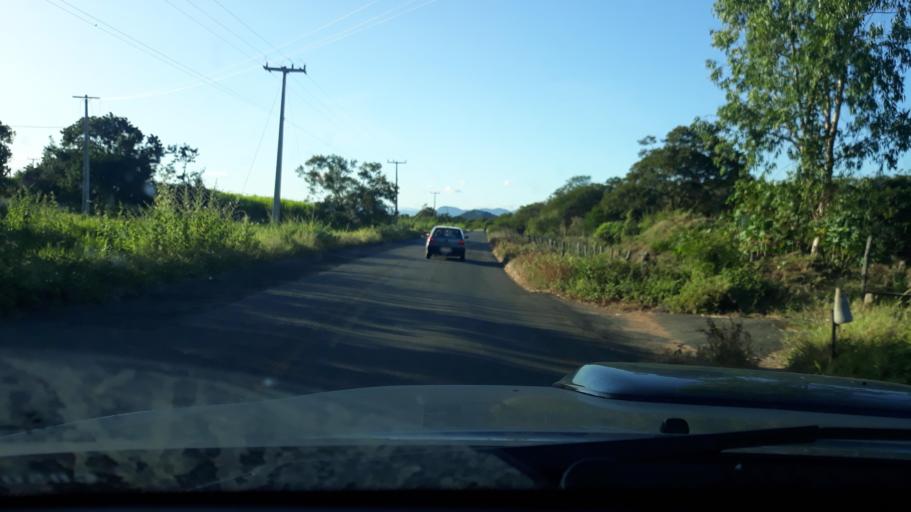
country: BR
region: Bahia
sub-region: Guanambi
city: Guanambi
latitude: -14.1418
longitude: -42.8440
